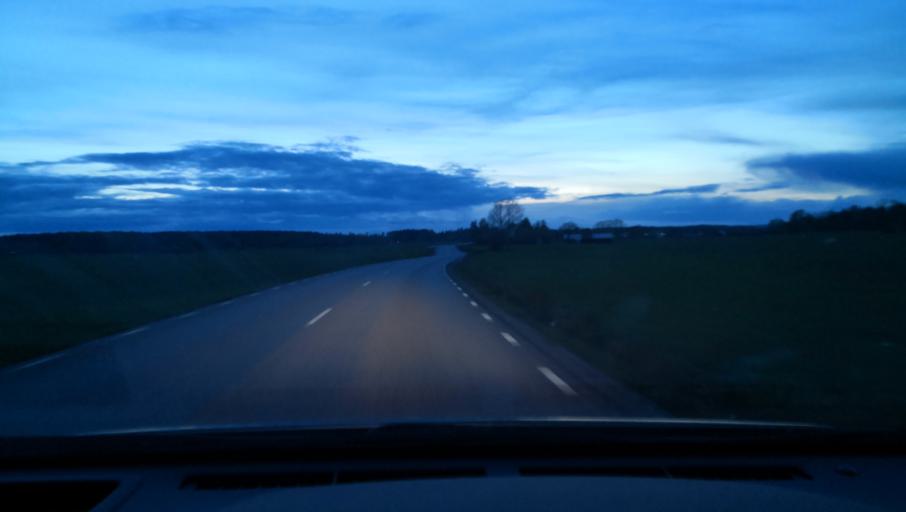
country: SE
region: OErebro
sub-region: Hallsbergs Kommun
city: Hallsberg
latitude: 59.1187
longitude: 15.0047
